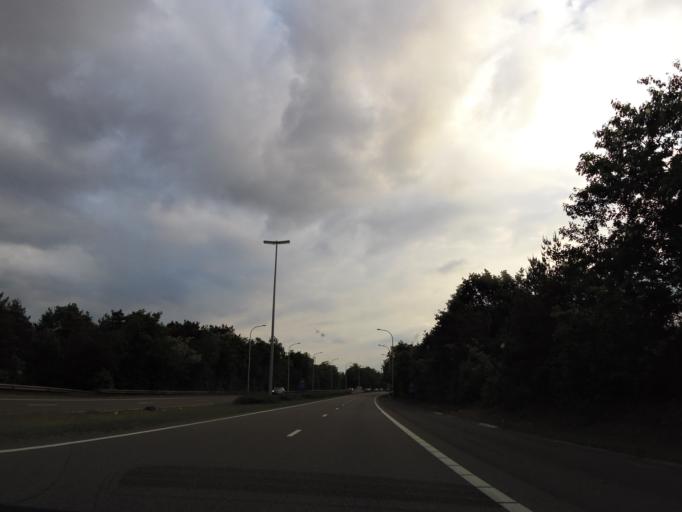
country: BE
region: Flanders
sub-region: Provincie Limburg
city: Genk
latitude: 50.9575
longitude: 5.4867
